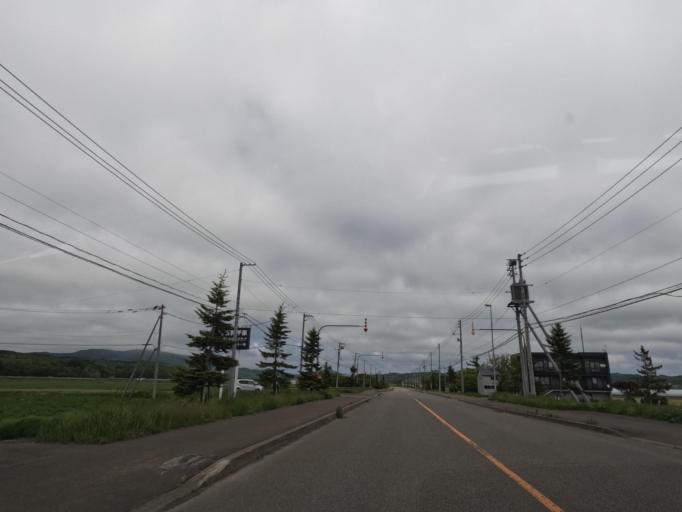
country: JP
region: Hokkaido
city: Tobetsu
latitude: 43.2499
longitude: 141.5200
